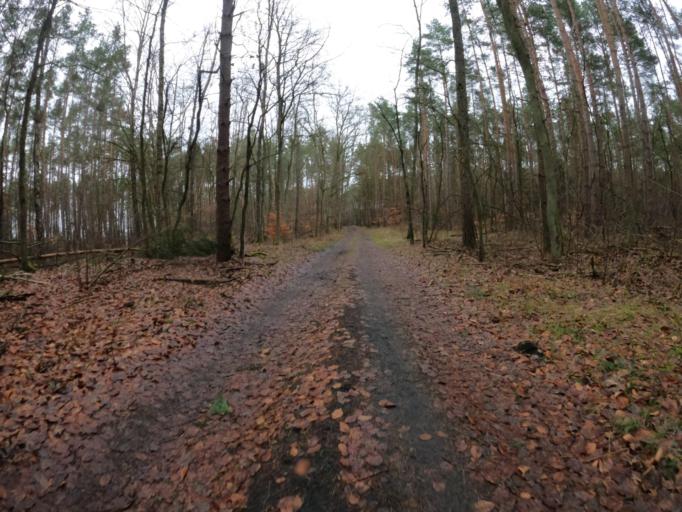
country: PL
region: West Pomeranian Voivodeship
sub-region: Powiat mysliborski
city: Debno
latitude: 52.7391
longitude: 14.7658
